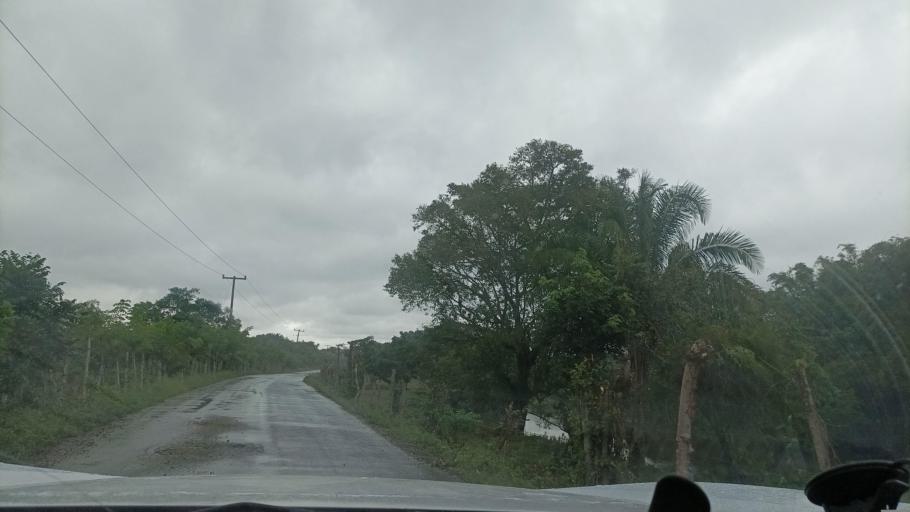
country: MX
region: Veracruz
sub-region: Moloacan
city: Cuichapa
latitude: 17.7578
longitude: -94.3943
